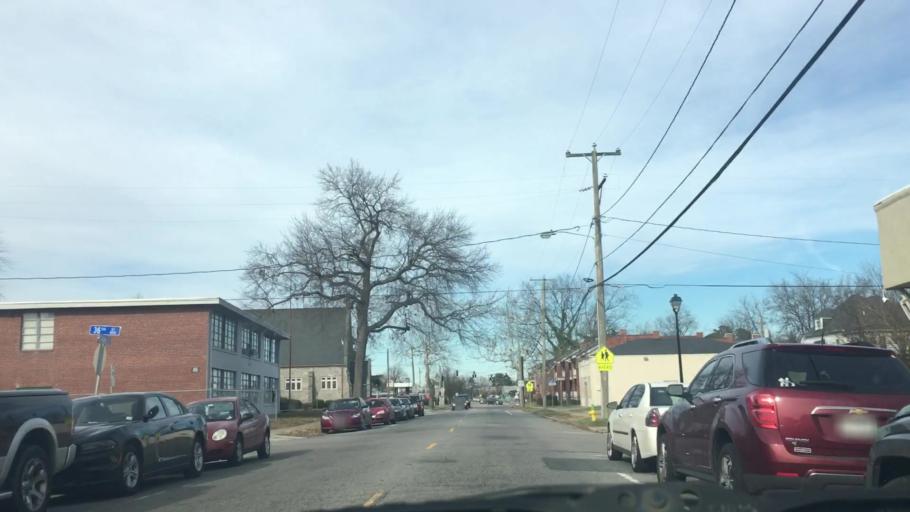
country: US
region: Virginia
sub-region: City of Norfolk
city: Norfolk
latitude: 36.8783
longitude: -76.2948
